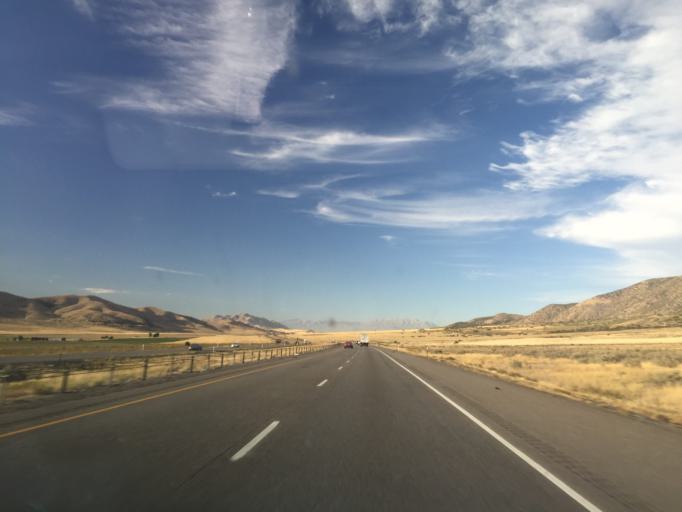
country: US
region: Utah
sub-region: Juab County
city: Mona
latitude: 39.8682
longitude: -111.8298
